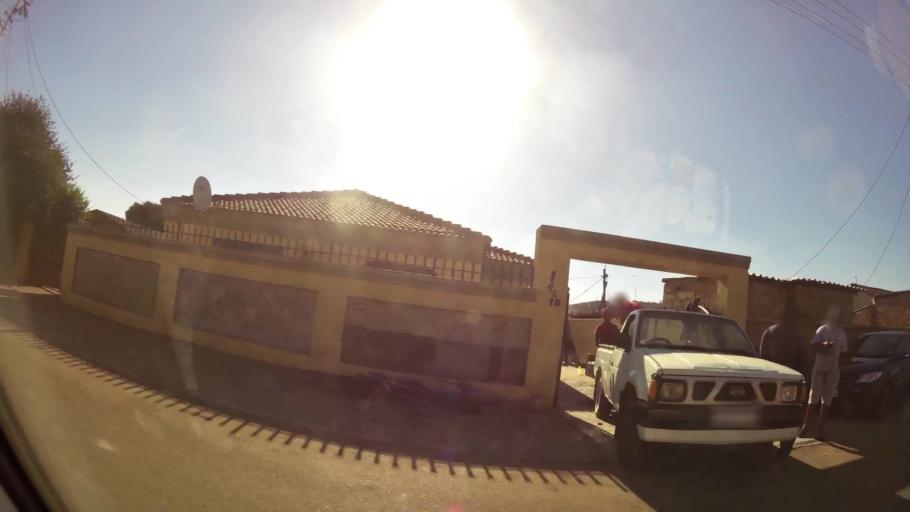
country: ZA
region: Gauteng
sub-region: City of Tshwane Metropolitan Municipality
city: Cullinan
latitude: -25.7117
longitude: 28.3828
